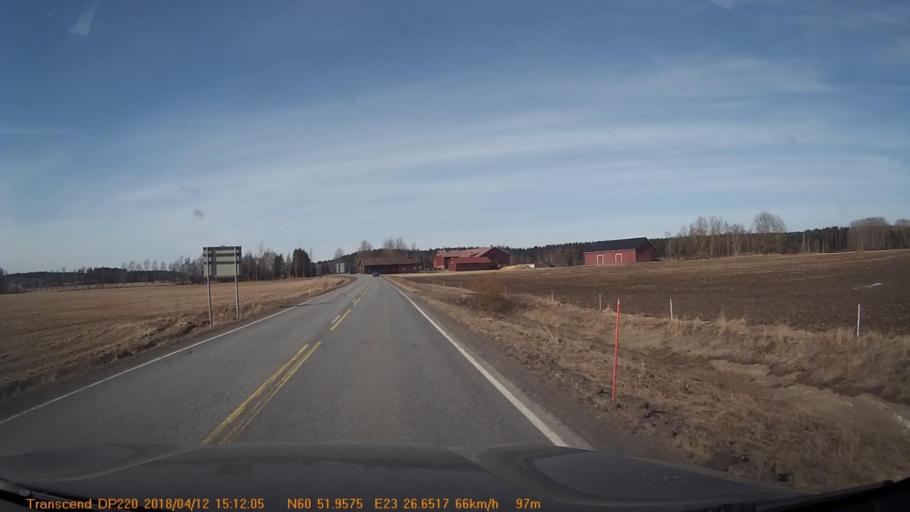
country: FI
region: Haeme
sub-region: Forssa
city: Jokioinen
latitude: 60.8661
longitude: 23.4441
